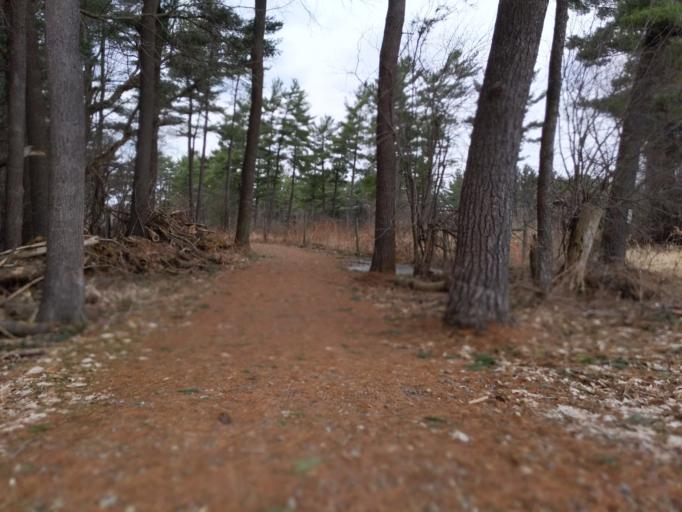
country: US
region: New York
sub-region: Tompkins County
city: Dryden
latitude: 42.4989
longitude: -76.3295
